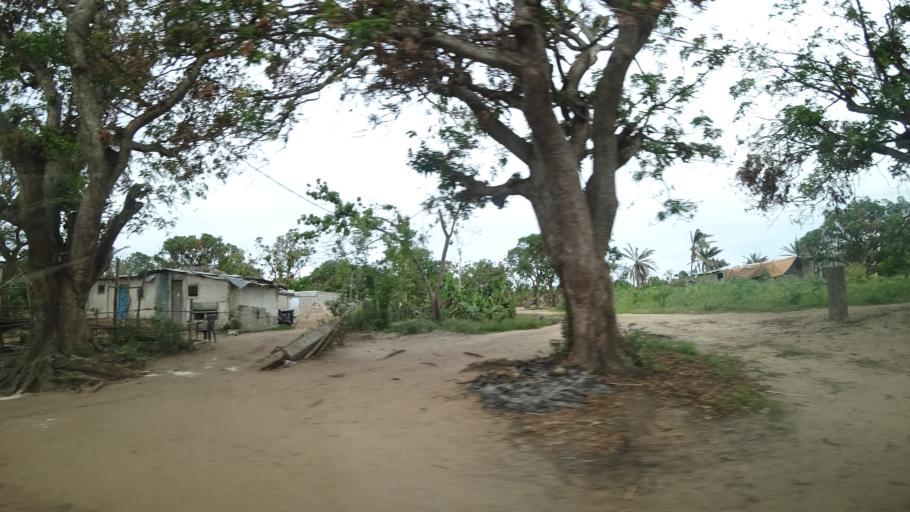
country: MZ
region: Sofala
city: Beira
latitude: -19.7175
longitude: 35.0050
